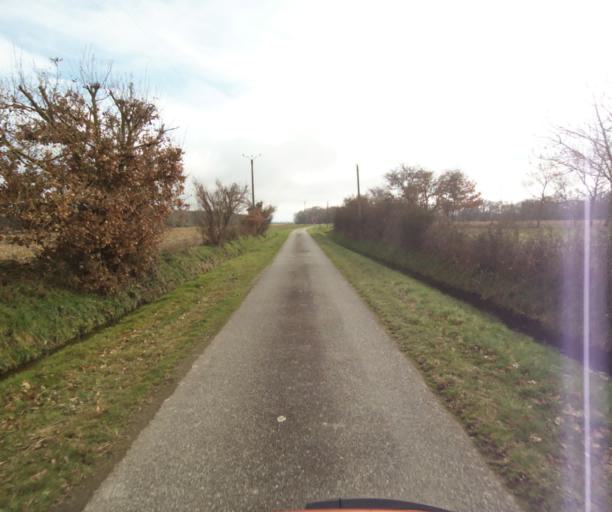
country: FR
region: Midi-Pyrenees
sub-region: Departement de l'Ariege
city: Mazeres
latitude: 43.2110
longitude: 1.6800
